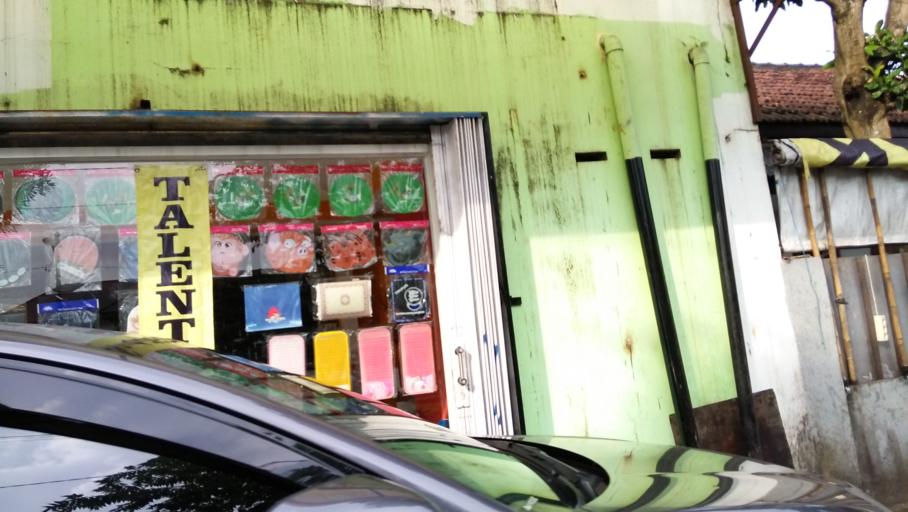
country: ID
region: Daerah Istimewa Yogyakarta
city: Yogyakarta
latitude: -7.7683
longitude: 110.3884
